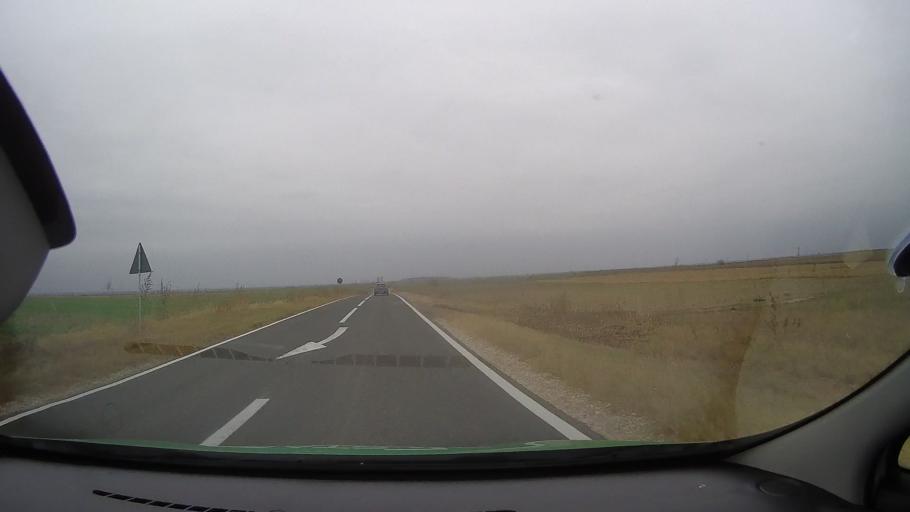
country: RO
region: Constanta
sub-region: Comuna Ciobanu
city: Ciobanu
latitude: 44.7021
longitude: 28.0200
